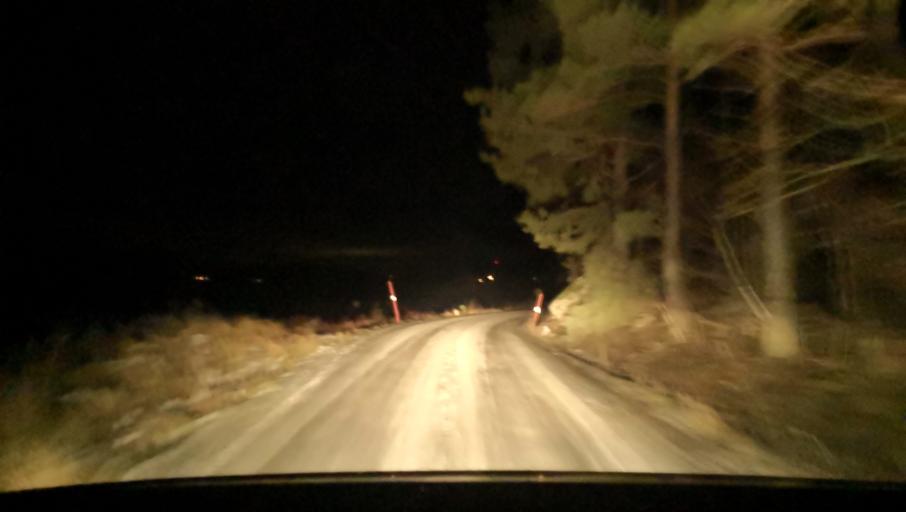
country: SE
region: Uppsala
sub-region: Enkopings Kommun
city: Irsta
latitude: 59.6444
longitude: 16.8697
